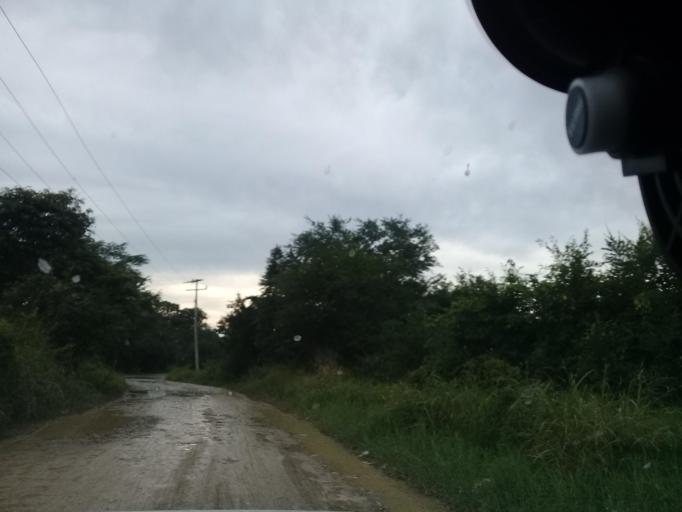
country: MX
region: Hidalgo
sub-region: Huejutla de Reyes
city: Parque de Poblamiento Solidaridad
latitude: 21.1558
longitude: -98.3773
